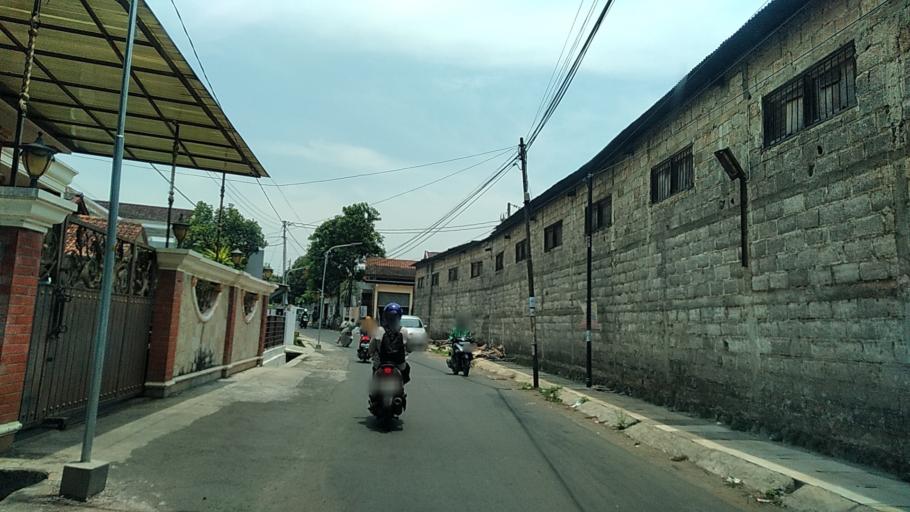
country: ID
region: Central Java
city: Semarang
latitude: -7.0634
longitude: 110.4115
